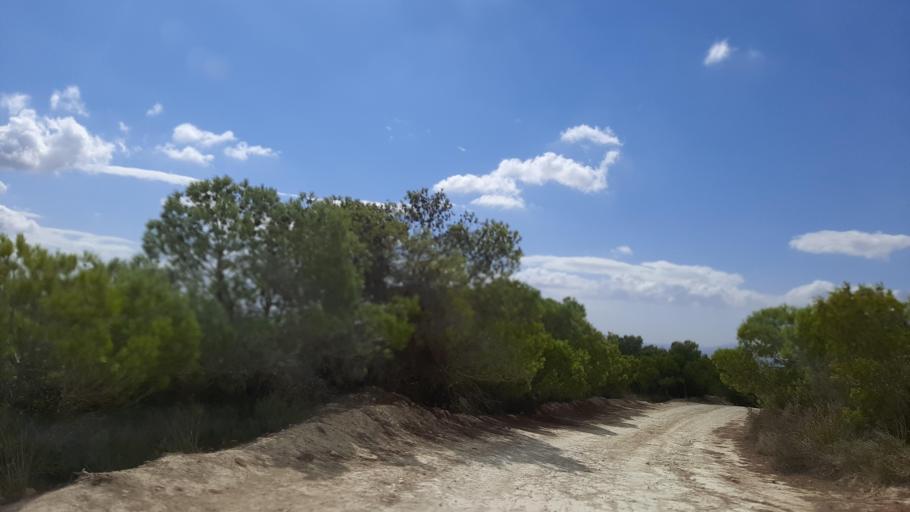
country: TN
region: Zaghwan
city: Zaghouan
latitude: 36.4926
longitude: 10.1762
